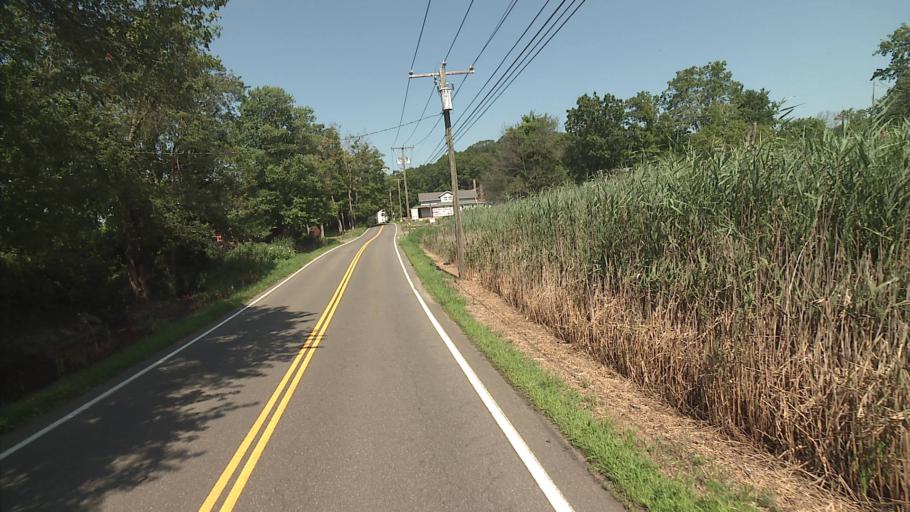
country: US
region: Connecticut
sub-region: New Haven County
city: Guilford
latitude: 41.2687
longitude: -72.7349
